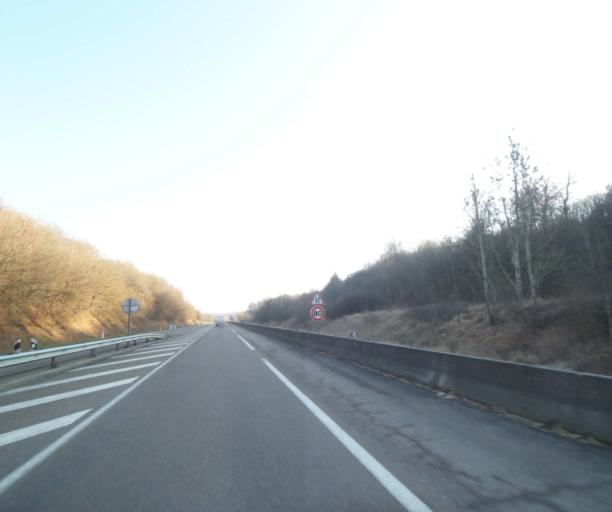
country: FR
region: Champagne-Ardenne
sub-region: Departement de la Haute-Marne
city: Chevillon
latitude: 48.5037
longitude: 5.1024
